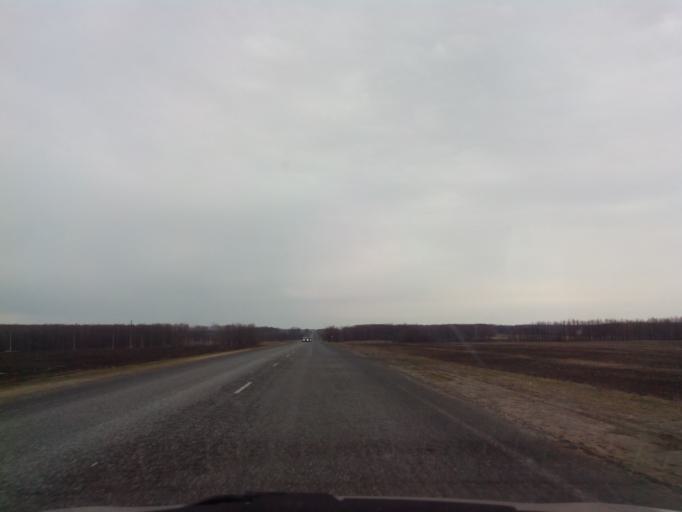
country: RU
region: Tambov
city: Zavoronezhskoye
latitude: 52.9921
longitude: 40.5541
